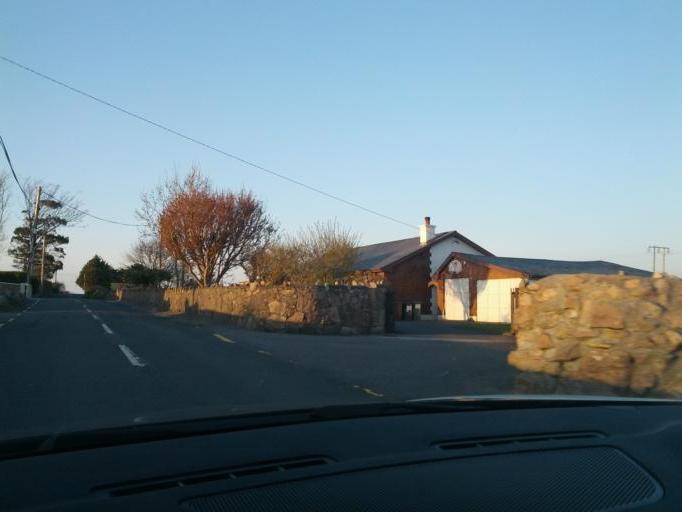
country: IE
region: Connaught
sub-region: County Galway
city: Gaillimh
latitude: 53.2808
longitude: -9.0830
